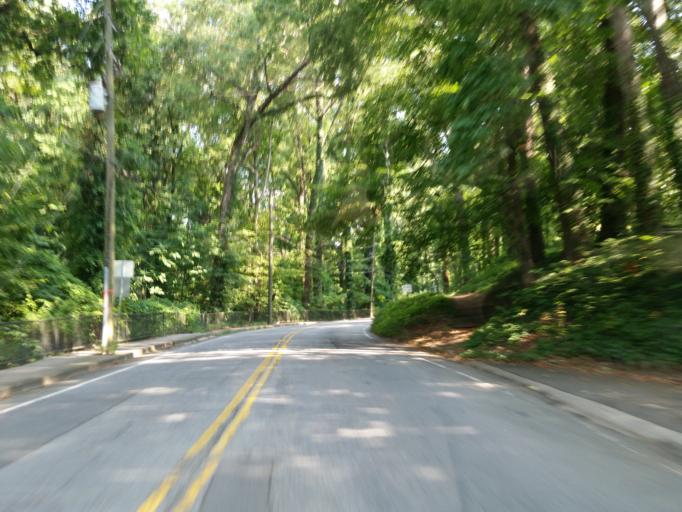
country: US
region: Georgia
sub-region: DeKalb County
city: North Atlanta
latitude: 33.8783
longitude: -84.3582
